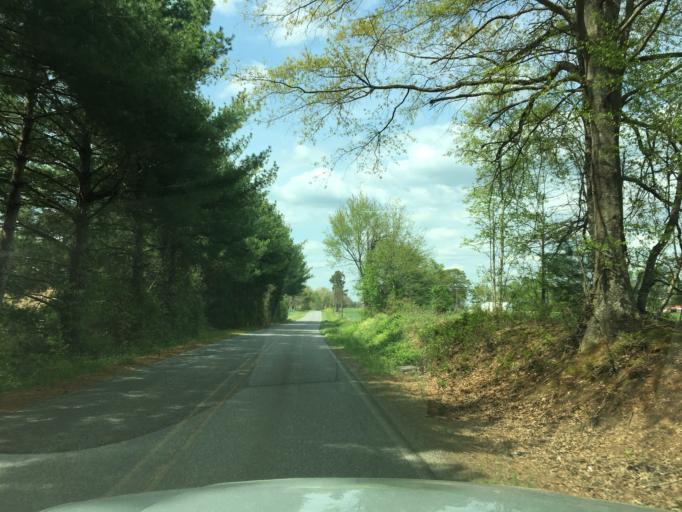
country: US
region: South Carolina
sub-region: Spartanburg County
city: Boiling Springs
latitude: 35.2003
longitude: -81.9706
